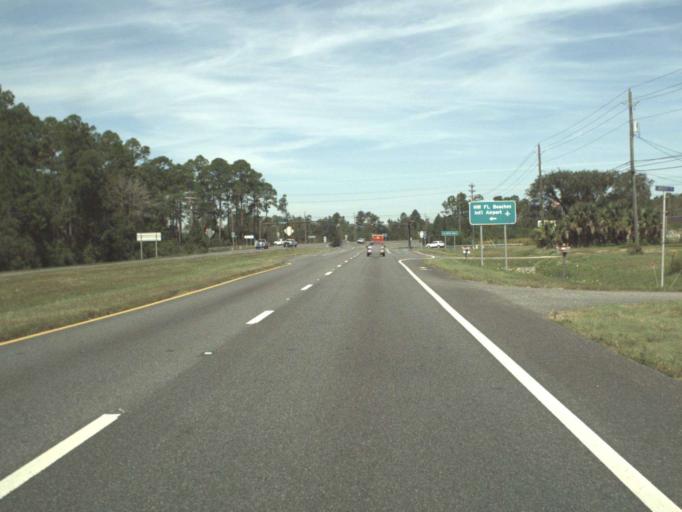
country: US
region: Florida
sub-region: Bay County
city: Lynn Haven
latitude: 30.3201
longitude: -85.6582
